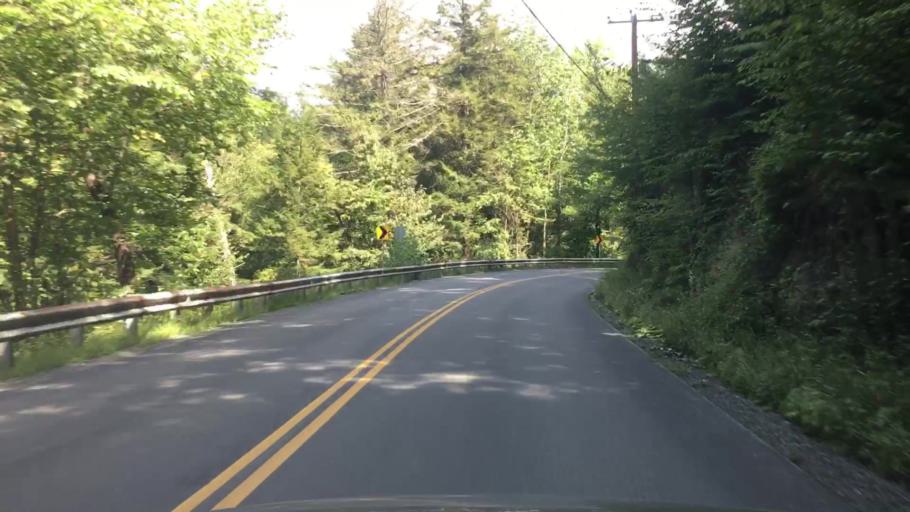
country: US
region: Vermont
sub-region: Windham County
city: West Brattleboro
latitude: 42.8082
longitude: -72.6125
